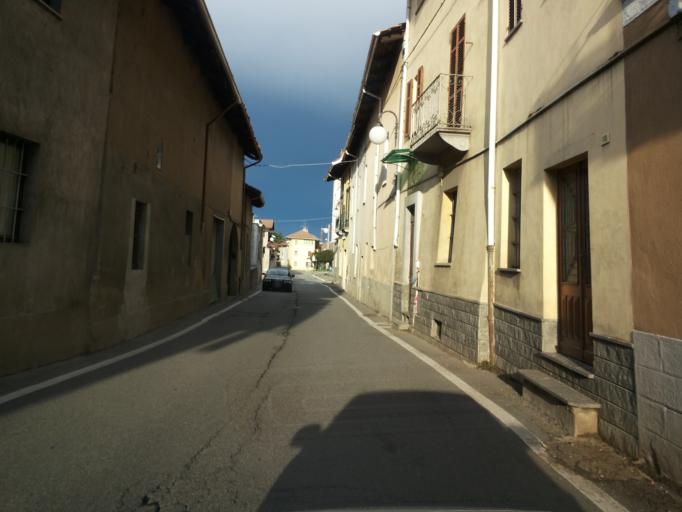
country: IT
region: Piedmont
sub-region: Provincia di Biella
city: Ponderano
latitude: 45.5382
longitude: 8.0565
